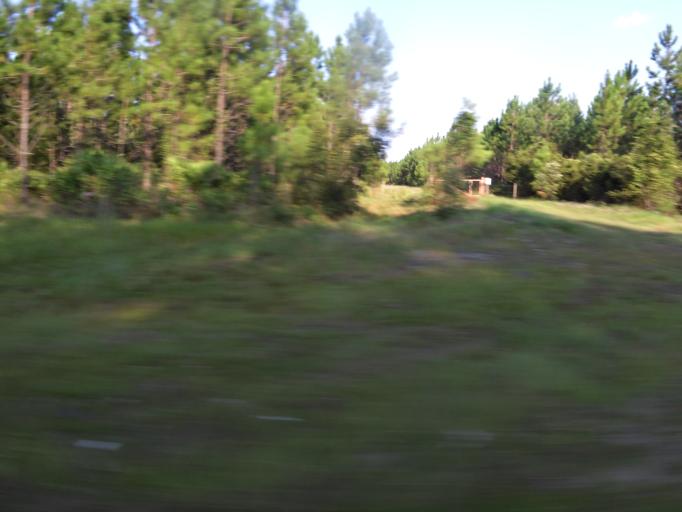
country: US
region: Florida
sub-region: Duval County
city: Baldwin
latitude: 30.3539
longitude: -82.0094
